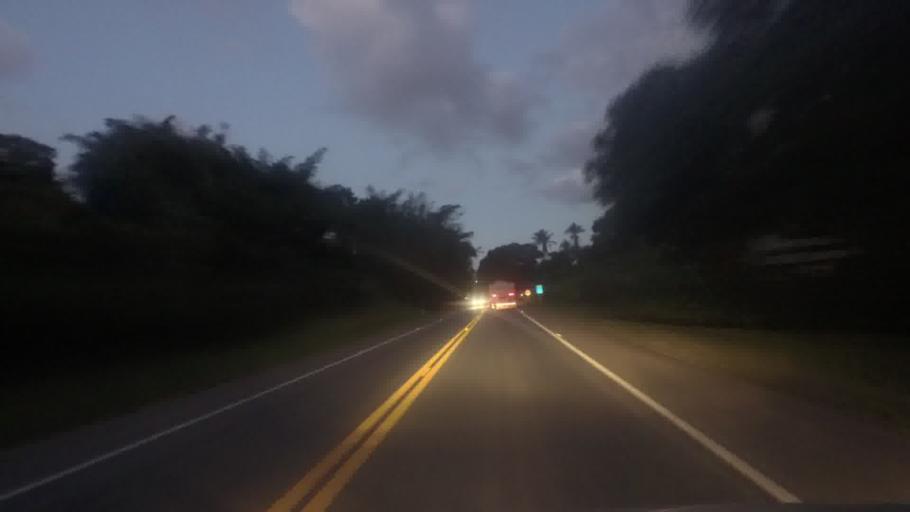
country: BR
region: Espirito Santo
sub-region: Iconha
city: Iconha
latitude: -20.7708
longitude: -40.7674
